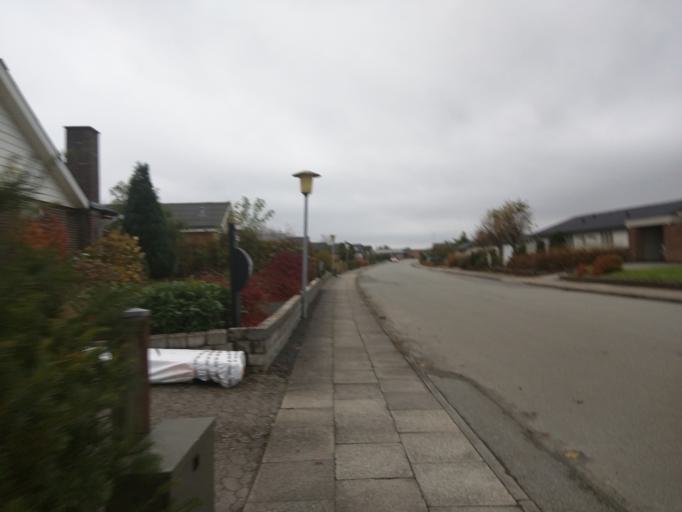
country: DK
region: Central Jutland
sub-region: Viborg Kommune
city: Viborg
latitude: 56.4672
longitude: 9.3856
